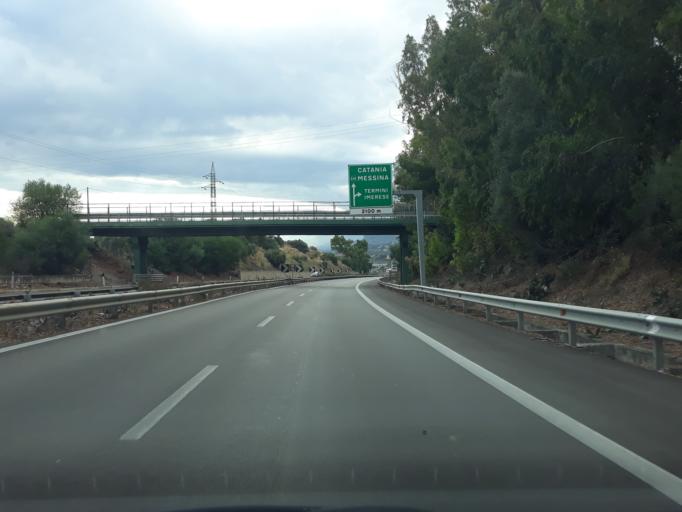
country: IT
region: Sicily
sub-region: Palermo
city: Termini Imerese
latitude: 37.9823
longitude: 13.6651
